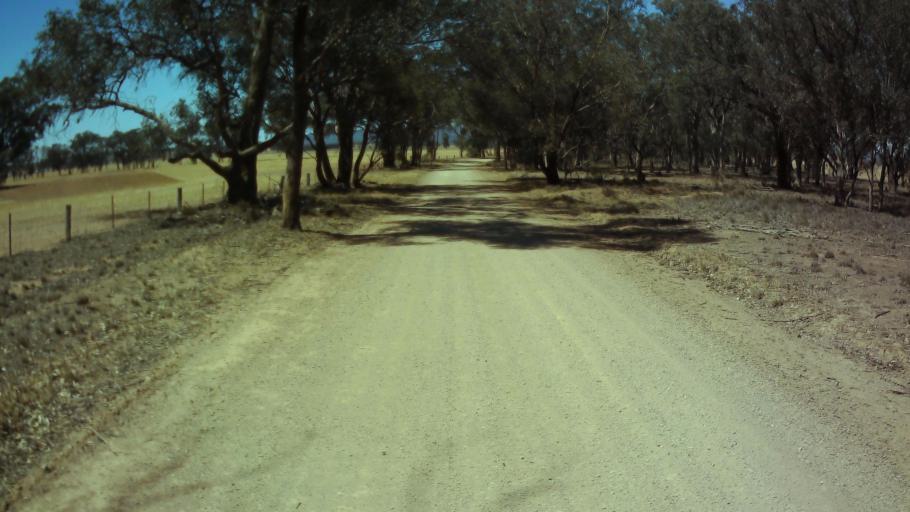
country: AU
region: New South Wales
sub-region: Weddin
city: Grenfell
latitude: -33.8873
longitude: 148.0876
